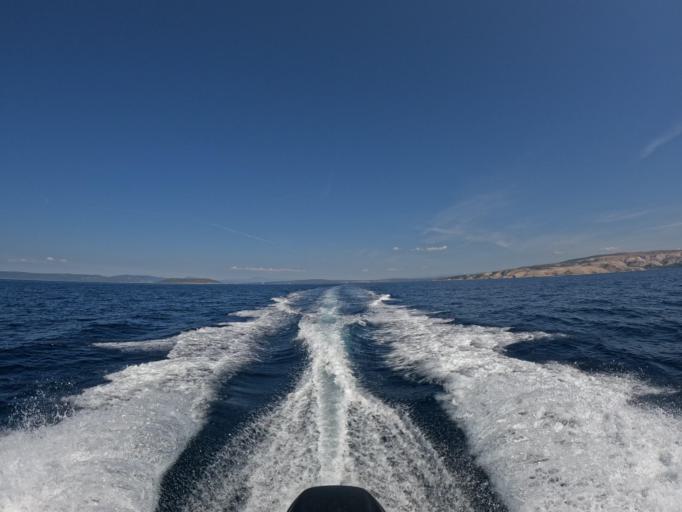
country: HR
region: Primorsko-Goranska
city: Punat
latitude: 44.9146
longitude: 14.6256
